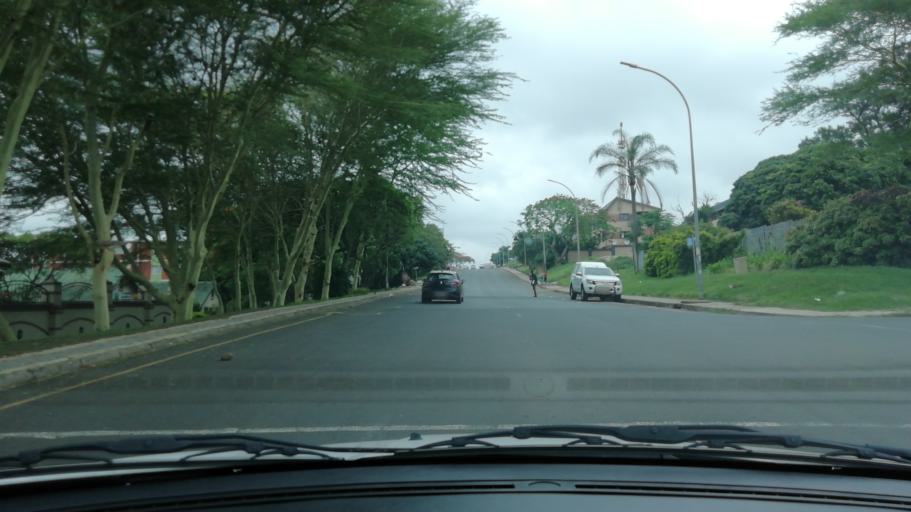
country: ZA
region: KwaZulu-Natal
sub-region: uThungulu District Municipality
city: Empangeni
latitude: -28.7422
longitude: 31.8945
